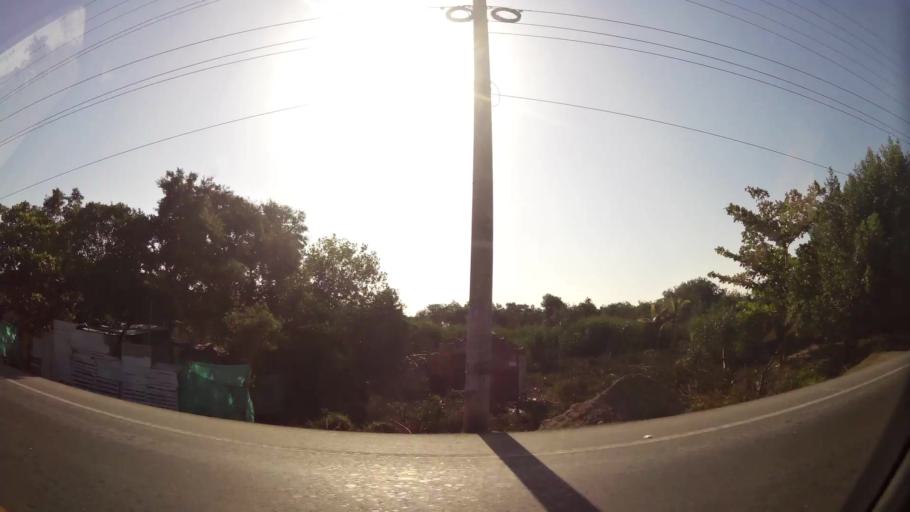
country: CO
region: Bolivar
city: Cartagena
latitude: 10.4707
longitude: -75.4965
